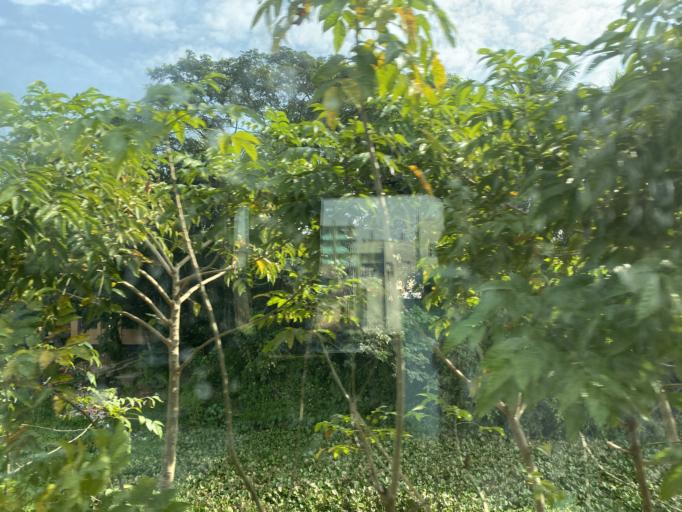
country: BD
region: Dhaka
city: Bhairab Bazar
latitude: 23.9640
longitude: 91.1174
